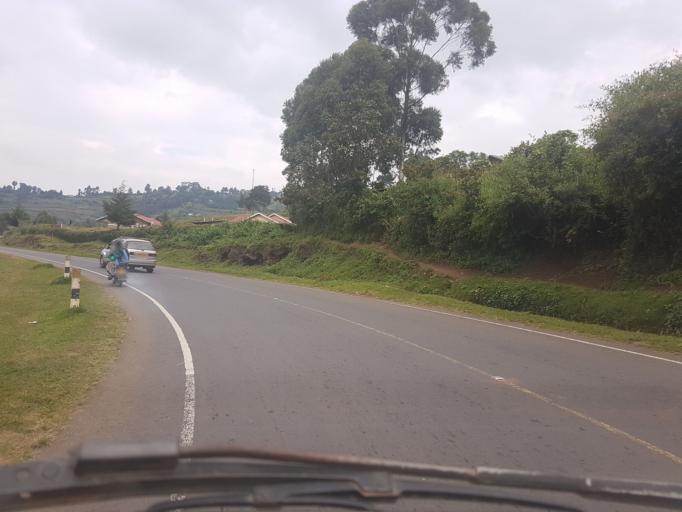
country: UG
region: Western Region
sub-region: Kisoro District
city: Kisoro
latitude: -1.2009
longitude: 29.8130
